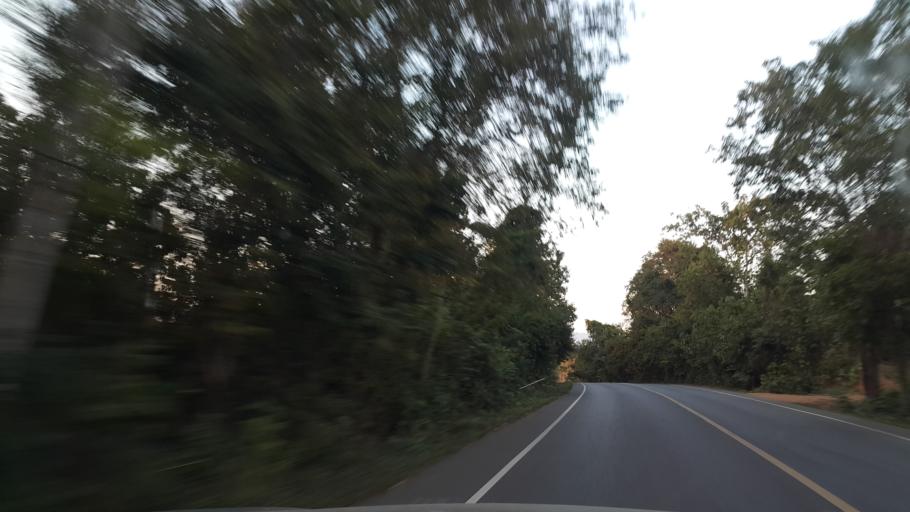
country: TH
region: Phrae
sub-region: Amphoe Wang Chin
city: Wang Chin
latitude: 17.8539
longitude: 99.6276
